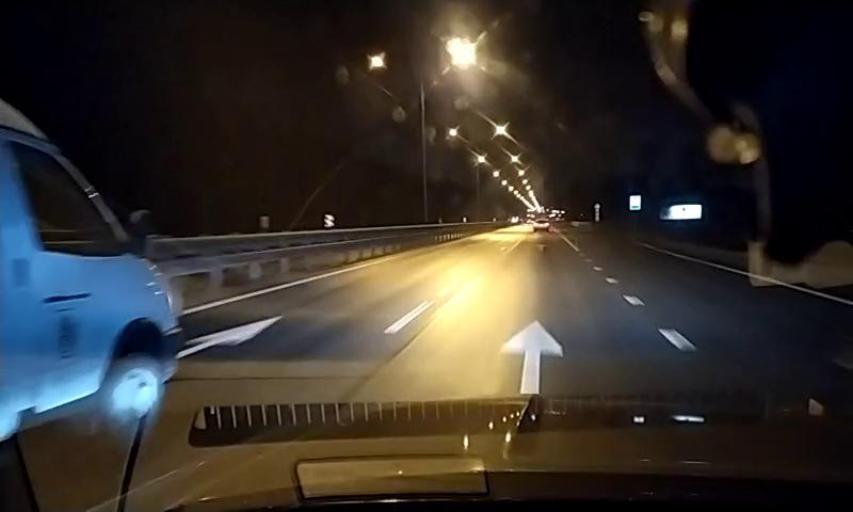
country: RU
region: Leningrad
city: Parnas
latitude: 60.1448
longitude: 30.3661
